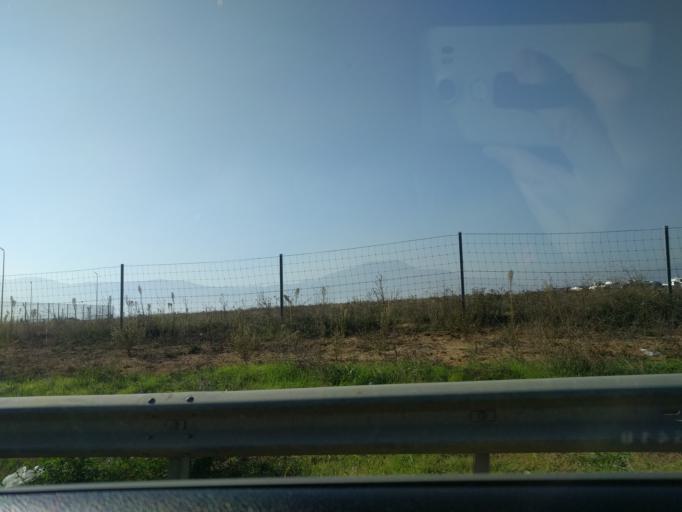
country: XK
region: Prizren
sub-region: Prizren
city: Prizren
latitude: 42.2506
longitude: 20.7087
